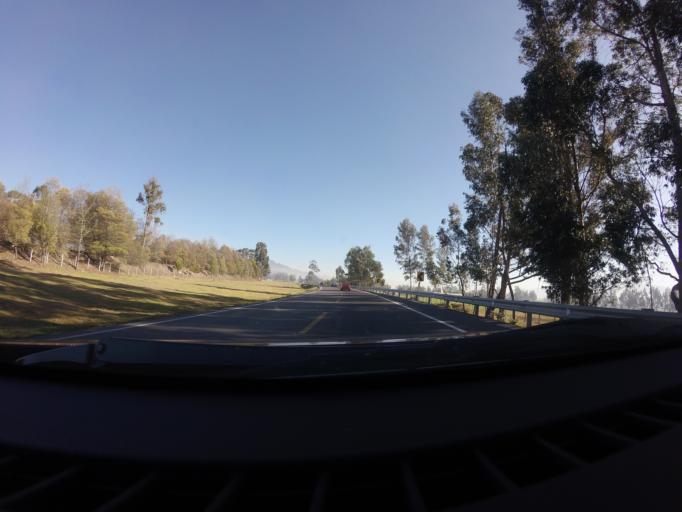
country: CO
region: Cundinamarca
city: Zipaquira
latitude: 5.0179
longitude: -73.9785
